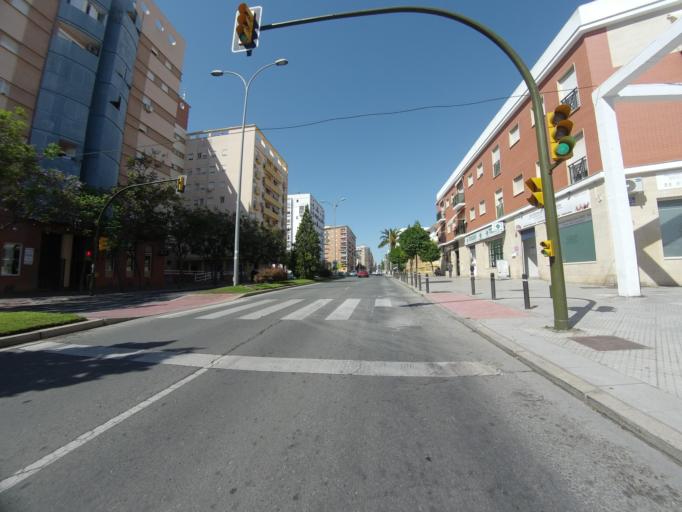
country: ES
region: Andalusia
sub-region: Provincia de Huelva
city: Huelva
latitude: 37.2616
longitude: -6.9292
